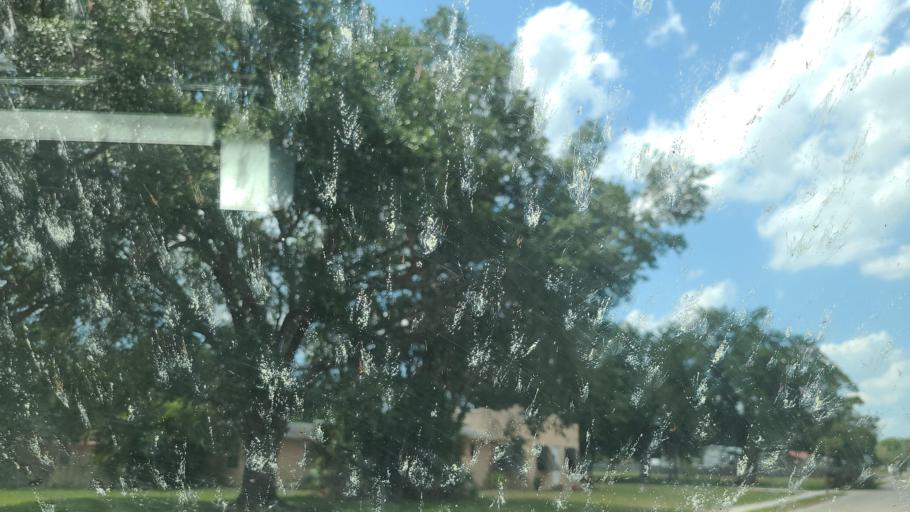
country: US
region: Florida
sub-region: Okeechobee County
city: Okeechobee
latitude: 27.2298
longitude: -80.8314
